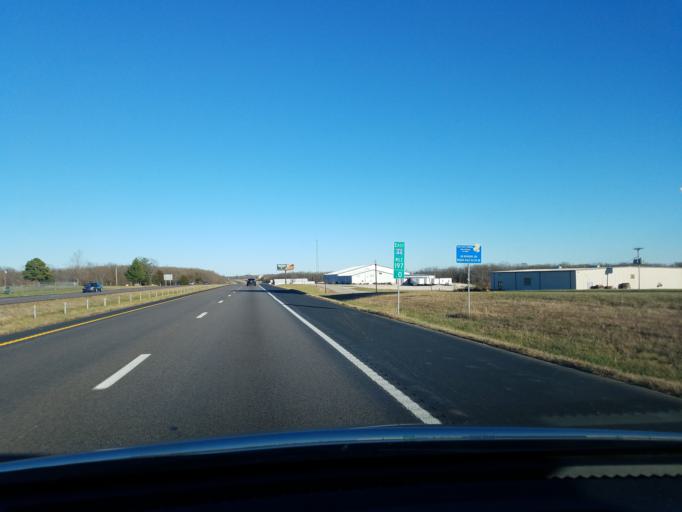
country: US
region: Missouri
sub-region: Phelps County
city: Saint James
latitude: 38.0115
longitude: -91.5984
